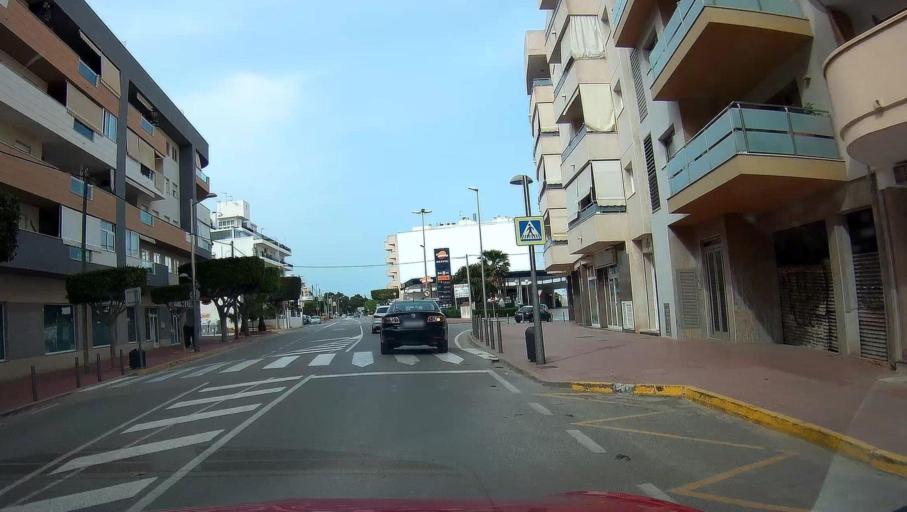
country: ES
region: Balearic Islands
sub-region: Illes Balears
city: Santa Eularia des Riu
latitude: 38.9874
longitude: 1.5383
